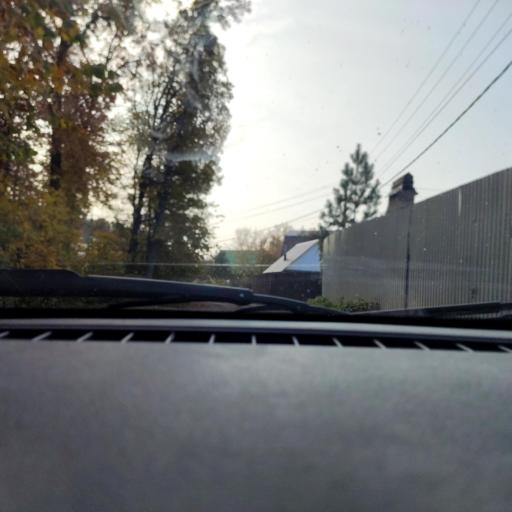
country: RU
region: Bashkortostan
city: Ufa
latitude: 54.6857
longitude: 55.8916
